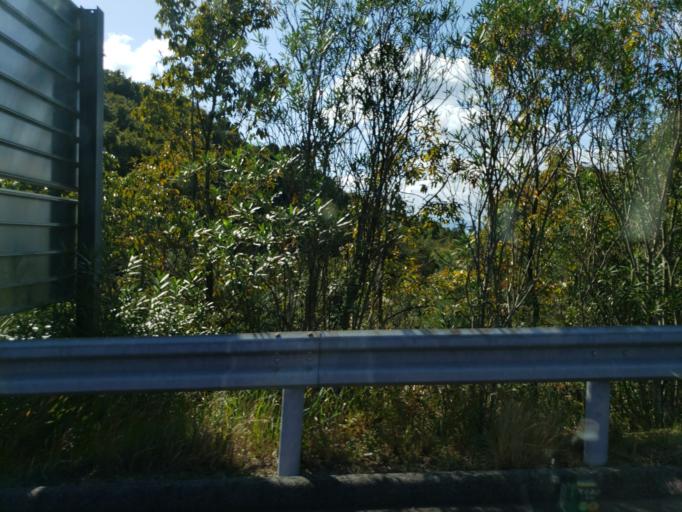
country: JP
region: Tokushima
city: Ishii
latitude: 34.1422
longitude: 134.4399
